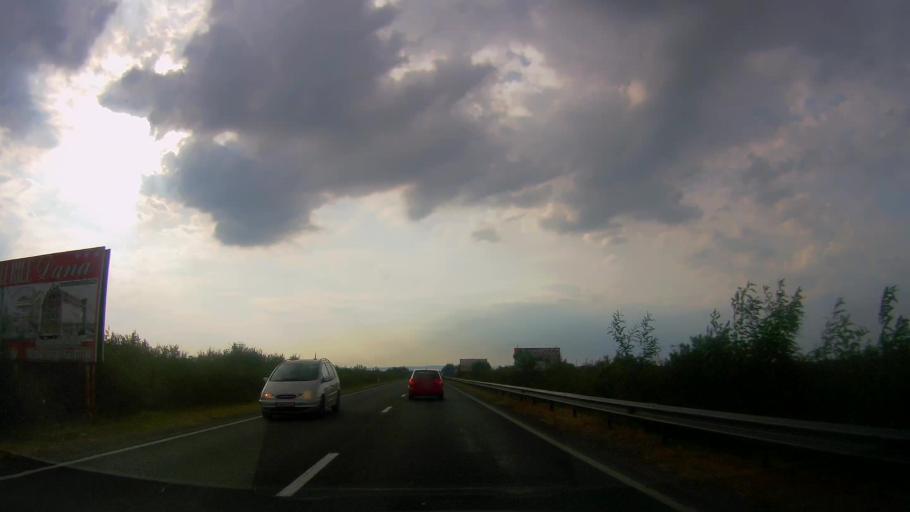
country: RO
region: Satu Mare
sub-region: Oras Ardud
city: Madaras
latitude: 47.7254
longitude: 22.8862
